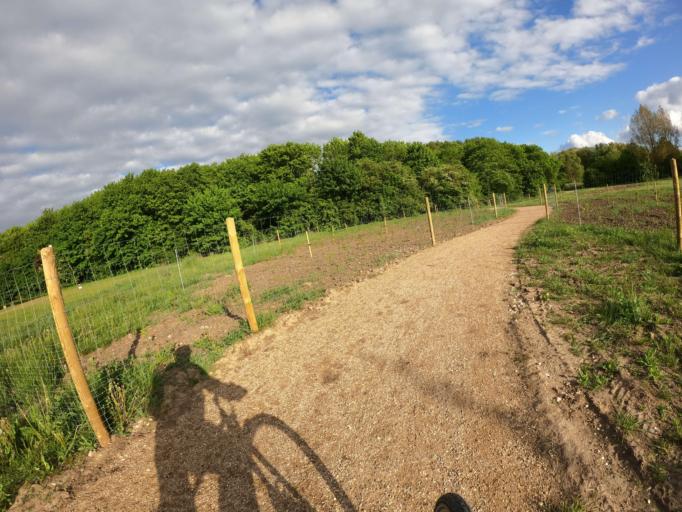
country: DK
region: Capital Region
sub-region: Ishoj Kommune
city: Ishoj
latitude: 55.6098
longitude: 12.3288
